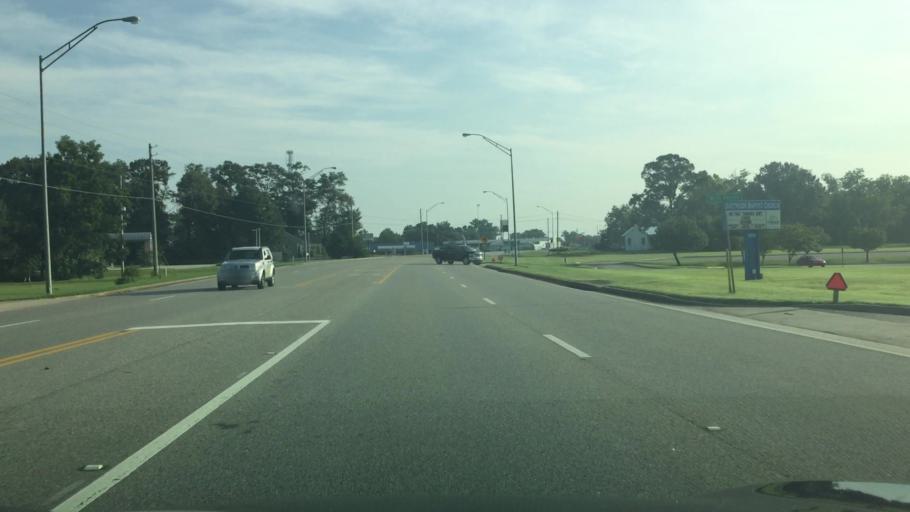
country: US
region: Alabama
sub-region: Covington County
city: Andalusia
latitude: 31.2903
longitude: -86.5032
